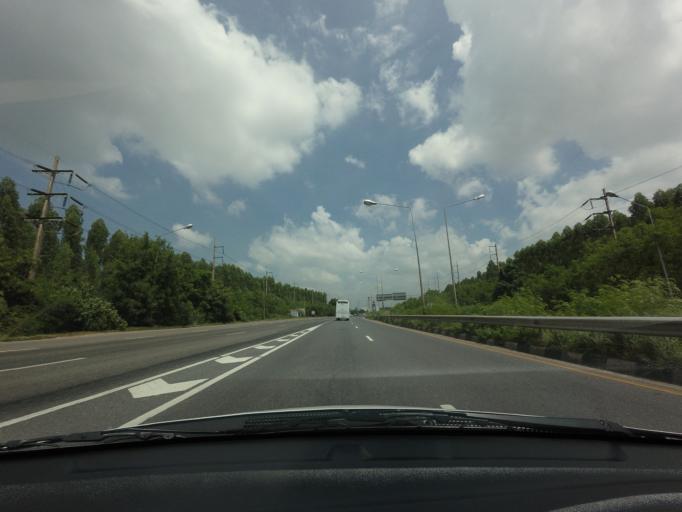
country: TH
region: Chachoengsao
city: Sanam Chai Khet
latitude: 13.7491
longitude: 101.4933
